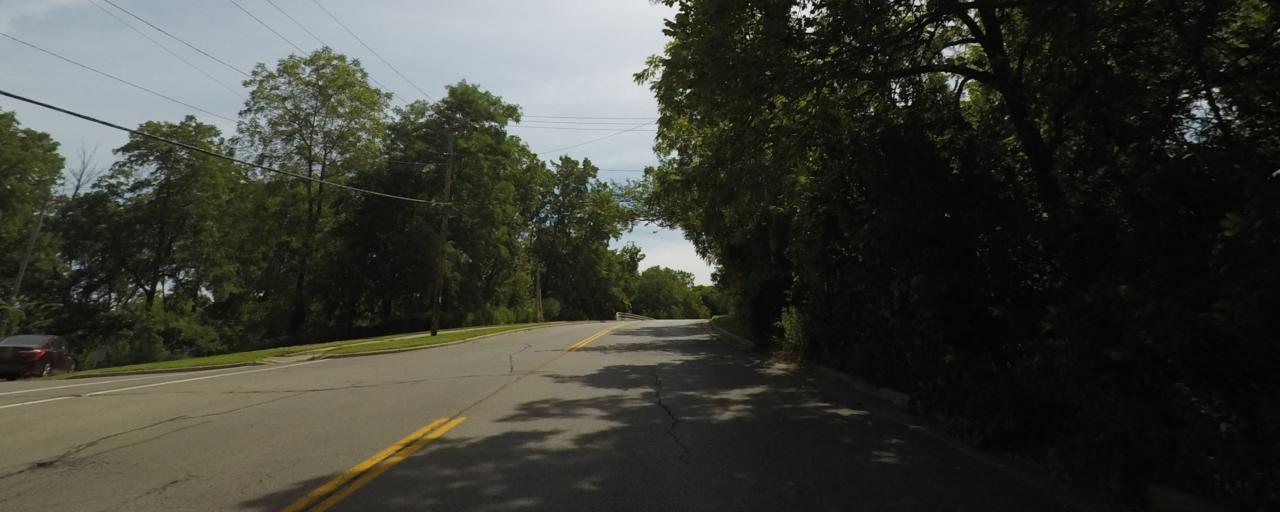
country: US
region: Wisconsin
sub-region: Dane County
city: Middleton
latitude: 43.0812
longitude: -89.4814
